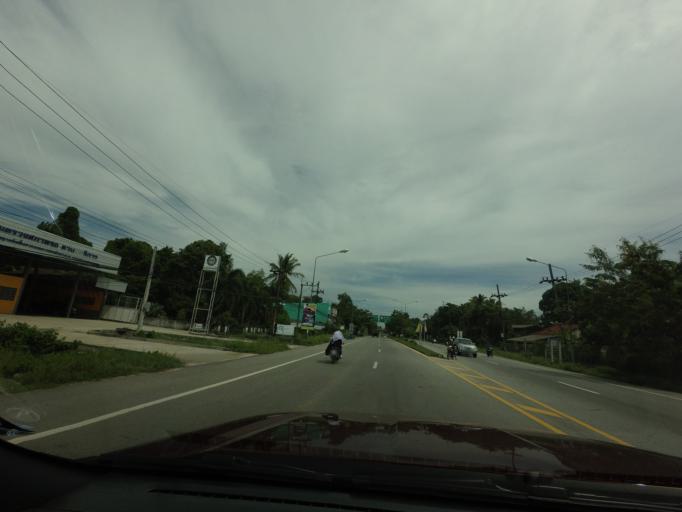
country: TH
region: Narathiwat
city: Tak Bai
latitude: 6.2580
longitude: 102.0466
